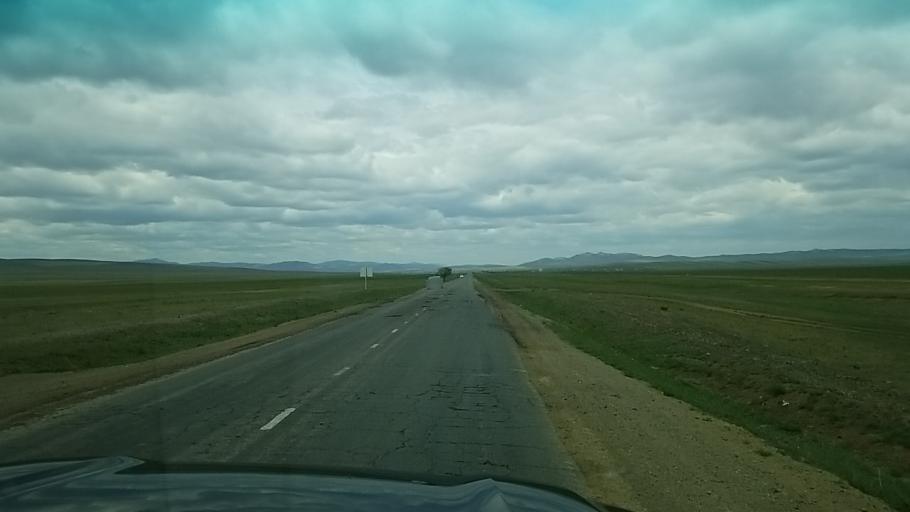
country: MN
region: Darhan Uul
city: Hongor
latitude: 49.2527
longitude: 106.0010
